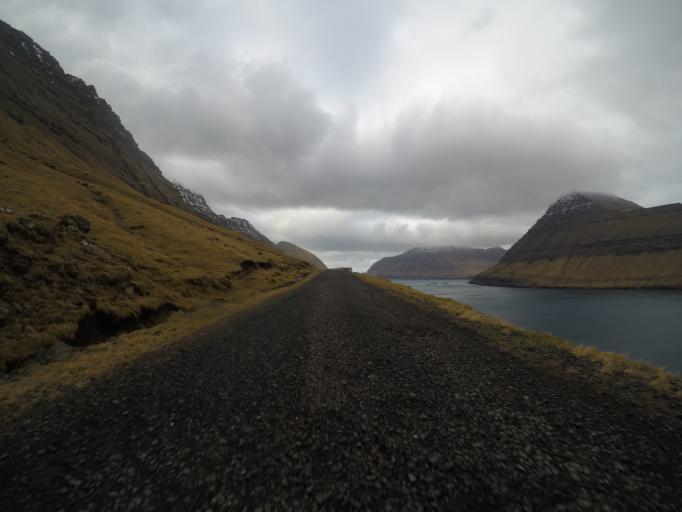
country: FO
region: Nordoyar
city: Klaksvik
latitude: 62.3225
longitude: -6.5613
